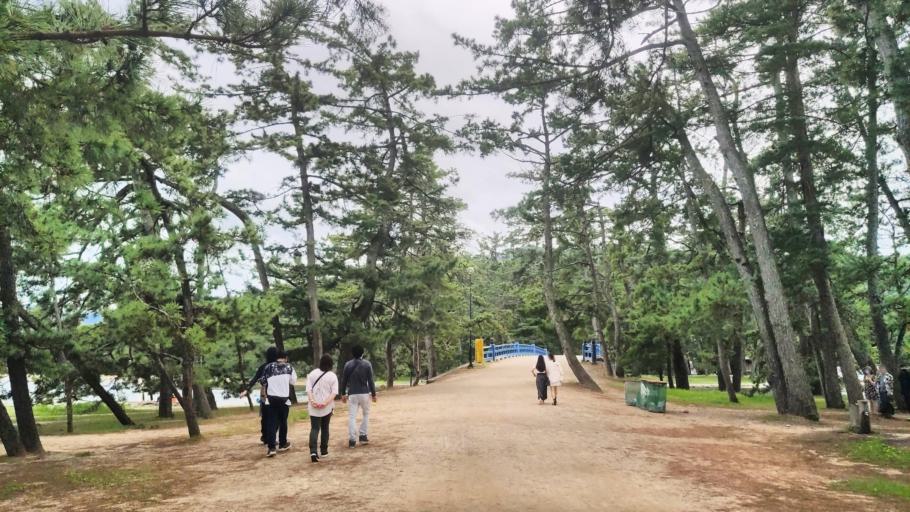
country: JP
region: Kyoto
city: Miyazu
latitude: 35.5592
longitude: 135.1869
